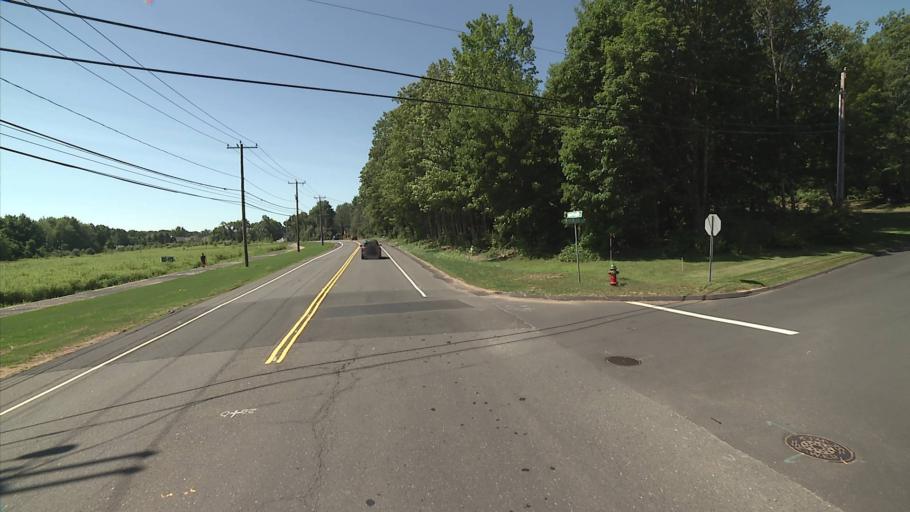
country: US
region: Connecticut
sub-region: Hartford County
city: Weatogue
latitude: 41.8248
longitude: -72.8280
